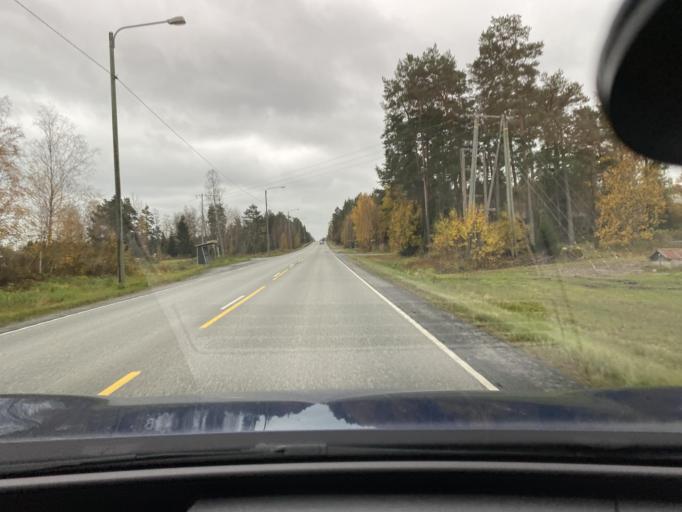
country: FI
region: Varsinais-Suomi
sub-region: Vakka-Suomi
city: Laitila
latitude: 60.9706
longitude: 21.5937
